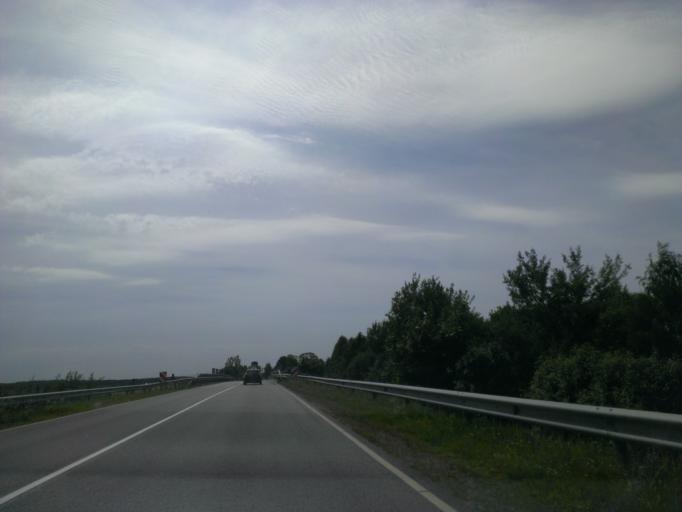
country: LV
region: Salaspils
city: Salaspils
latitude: 56.8537
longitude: 24.4007
